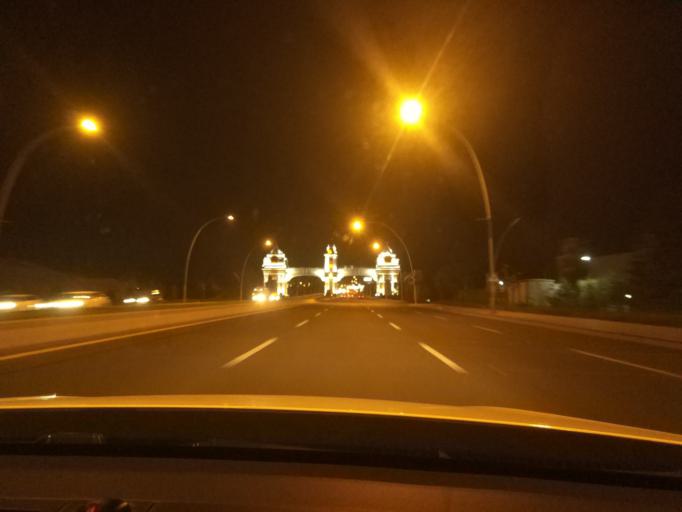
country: TR
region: Ankara
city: Mamak
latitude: 40.0743
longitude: 32.9487
